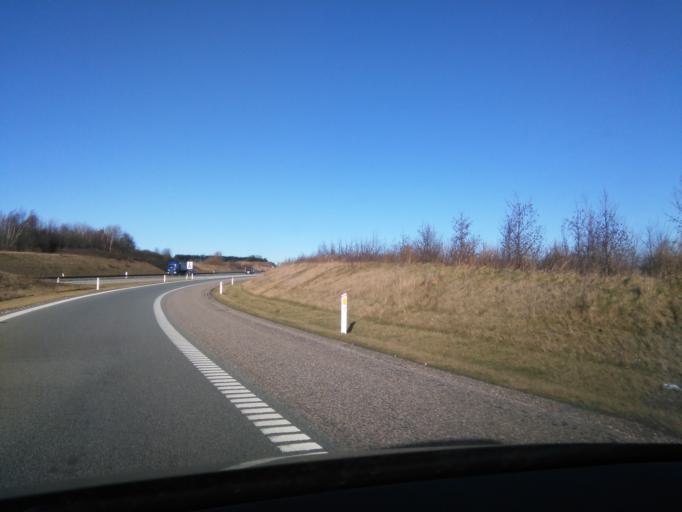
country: DK
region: Central Jutland
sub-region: Arhus Kommune
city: Trige
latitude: 56.2258
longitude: 10.1216
